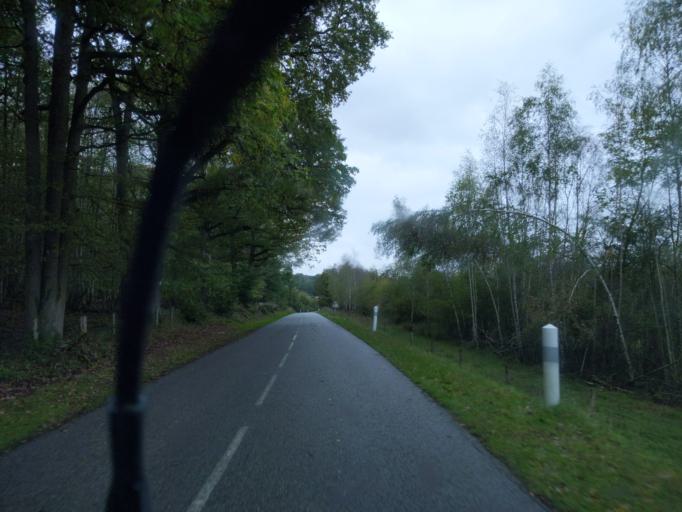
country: FR
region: Ile-de-France
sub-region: Departement des Yvelines
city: Bullion
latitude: 48.6312
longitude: 1.9618
